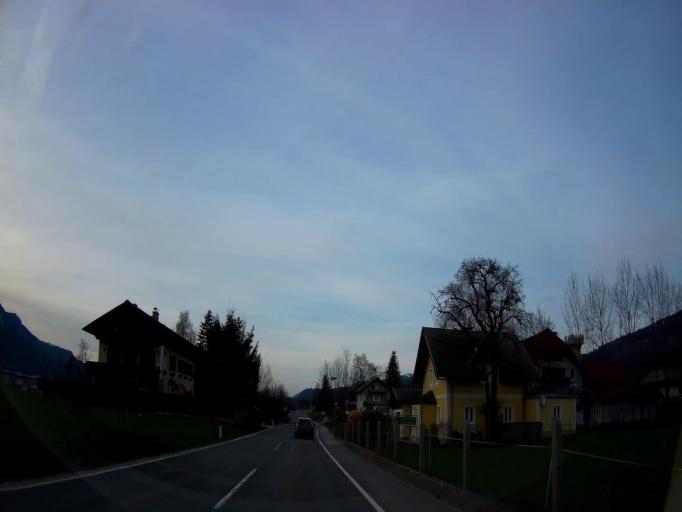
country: AT
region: Salzburg
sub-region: Politischer Bezirk Hallein
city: Golling an der Salzach
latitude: 47.6065
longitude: 13.1679
